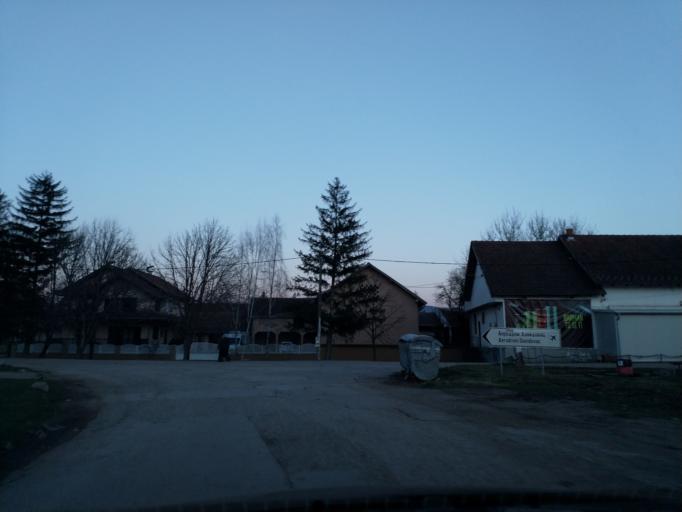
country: RS
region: Central Serbia
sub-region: Pomoravski Okrug
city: Paracin
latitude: 43.8653
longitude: 21.4751
